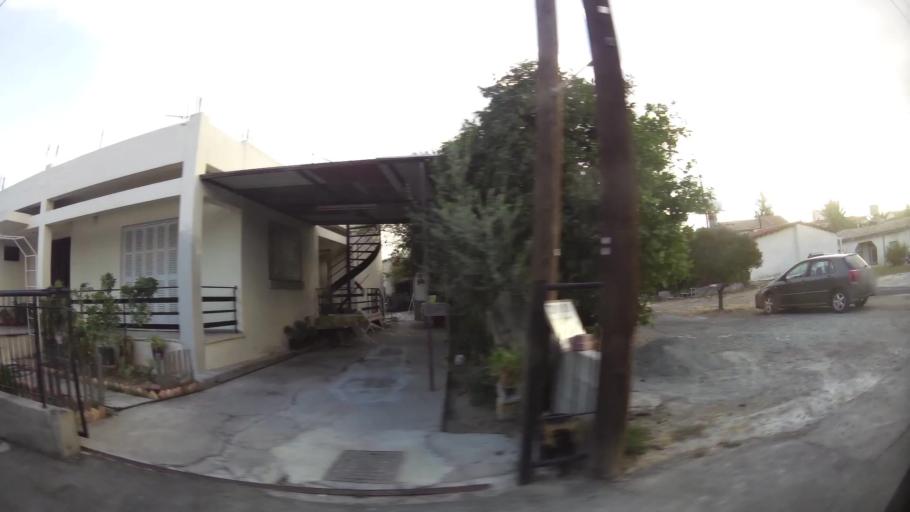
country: CY
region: Lefkosia
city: Kato Deftera
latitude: 35.1177
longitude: 33.3022
